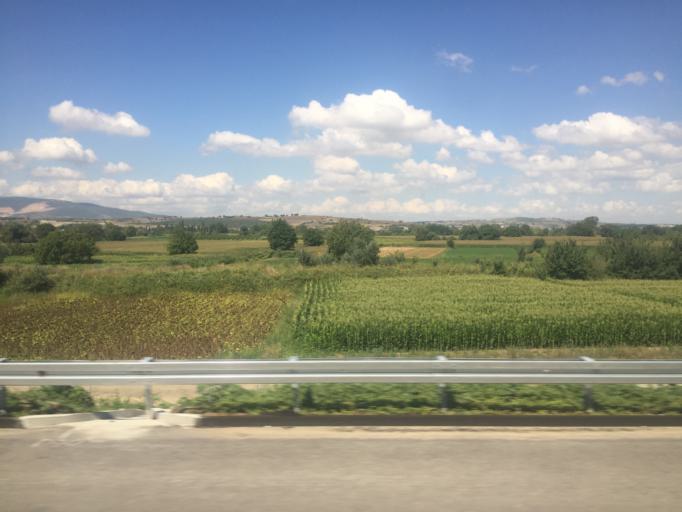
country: TR
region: Balikesir
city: Gobel
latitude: 39.9967
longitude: 28.1917
